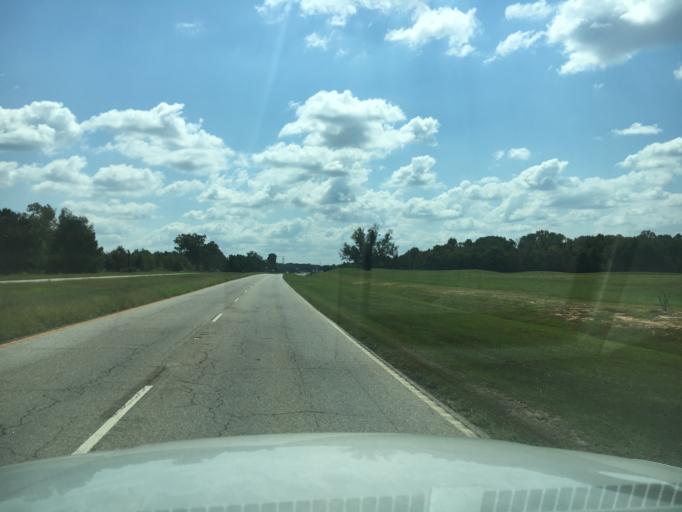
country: US
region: South Carolina
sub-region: Greenwood County
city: Ware Shoals
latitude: 34.3115
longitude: -82.2224
